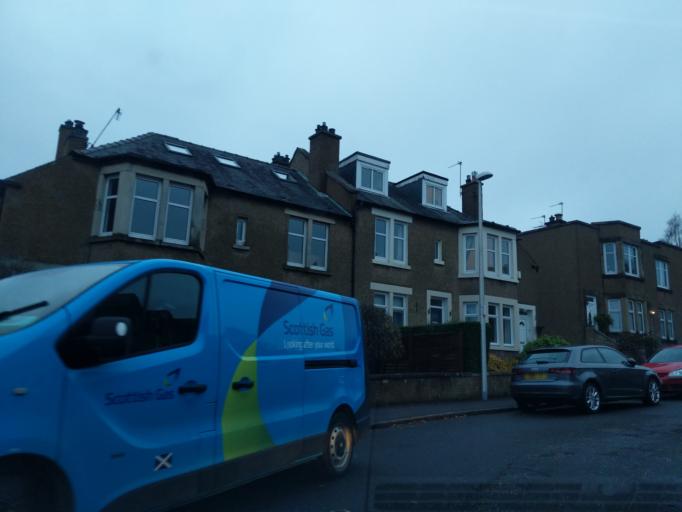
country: GB
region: Scotland
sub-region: Edinburgh
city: Colinton
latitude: 55.9447
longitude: -3.2873
